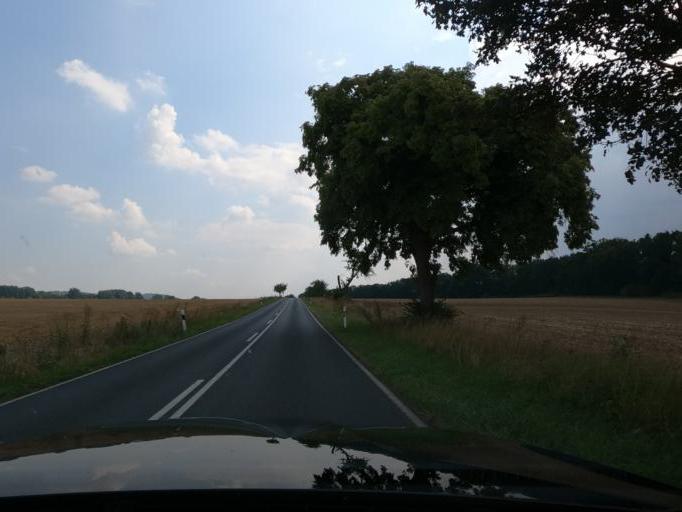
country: DE
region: Lower Saxony
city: Alt Wallmoden
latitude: 52.0312
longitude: 10.3320
